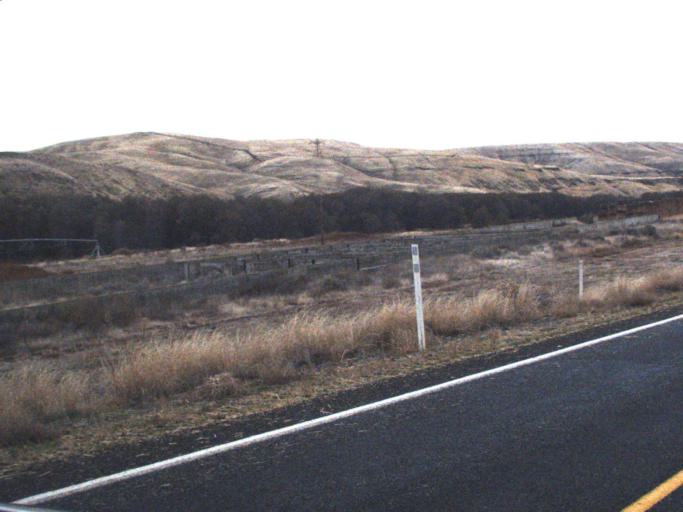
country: US
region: Washington
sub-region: Walla Walla County
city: Waitsburg
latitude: 46.5339
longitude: -118.1456
